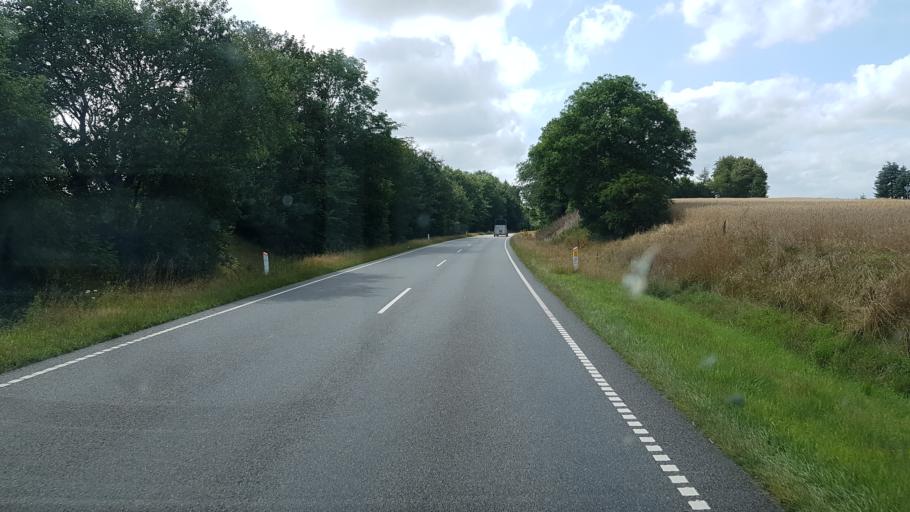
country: DK
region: South Denmark
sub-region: Vejen Kommune
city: Vejen
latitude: 55.5485
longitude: 9.1001
